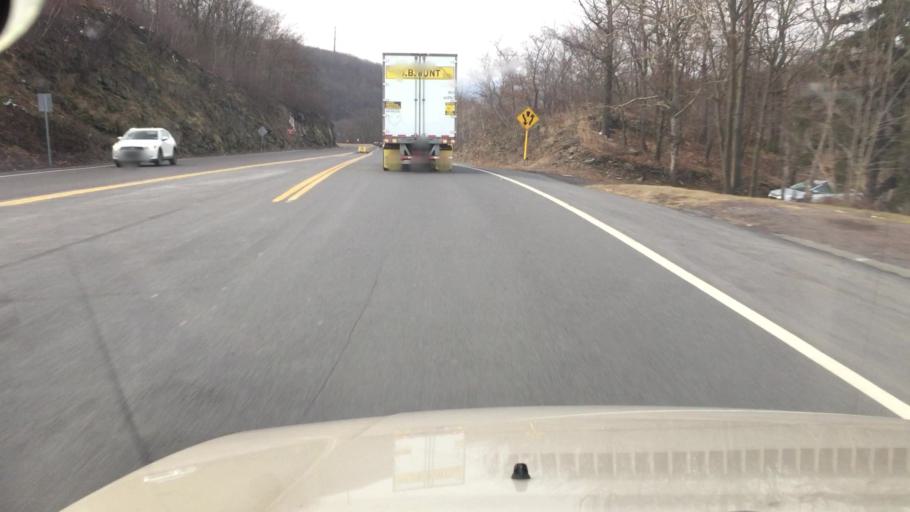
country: US
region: Pennsylvania
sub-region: Luzerne County
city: Mountain Top
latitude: 41.1783
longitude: -75.8833
